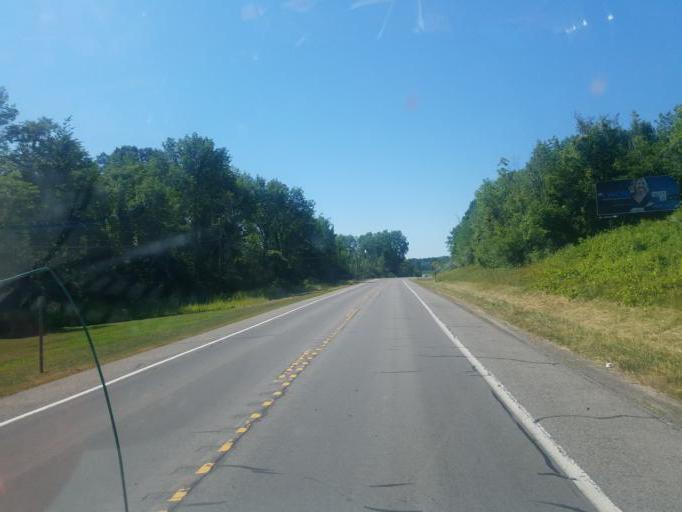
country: US
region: New York
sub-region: Wayne County
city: Newark
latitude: 42.9988
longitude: -77.0924
